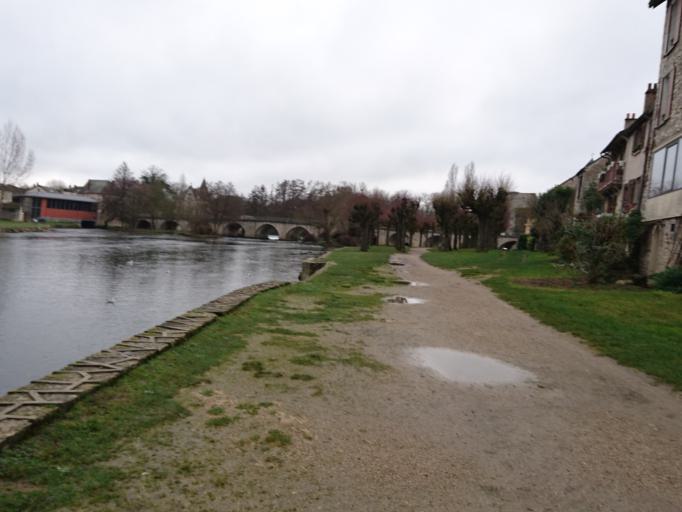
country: FR
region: Ile-de-France
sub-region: Departement de Seine-et-Marne
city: Moret-sur-Loing
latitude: 48.3741
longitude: 2.8189
